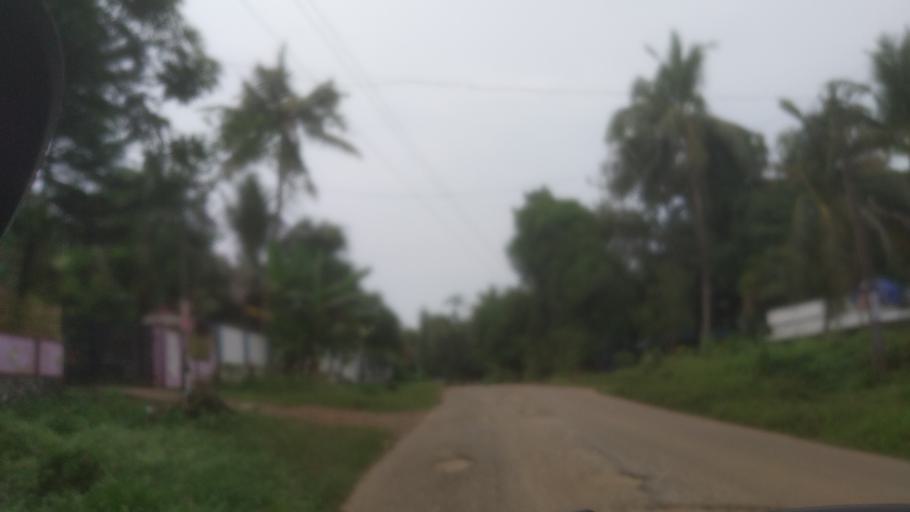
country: IN
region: Kerala
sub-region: Ernakulam
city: Perumbavoor
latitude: 10.0542
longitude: 76.5197
